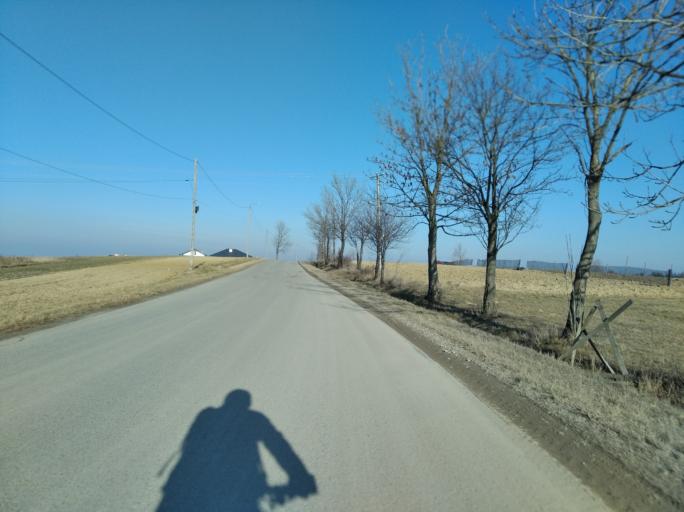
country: PL
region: Subcarpathian Voivodeship
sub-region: Powiat rzeszowski
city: Straszydle
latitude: 49.8794
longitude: 21.9855
